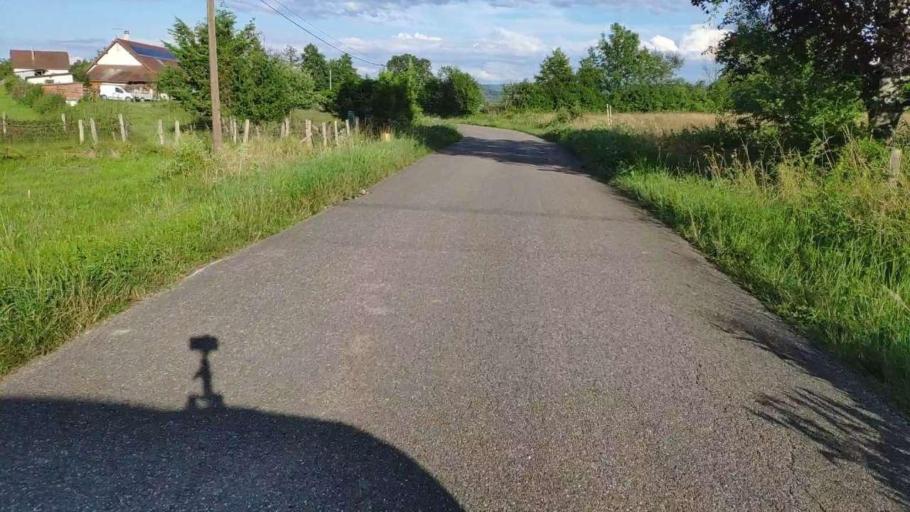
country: FR
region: Franche-Comte
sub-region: Departement du Jura
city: Bletterans
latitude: 46.7821
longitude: 5.4855
